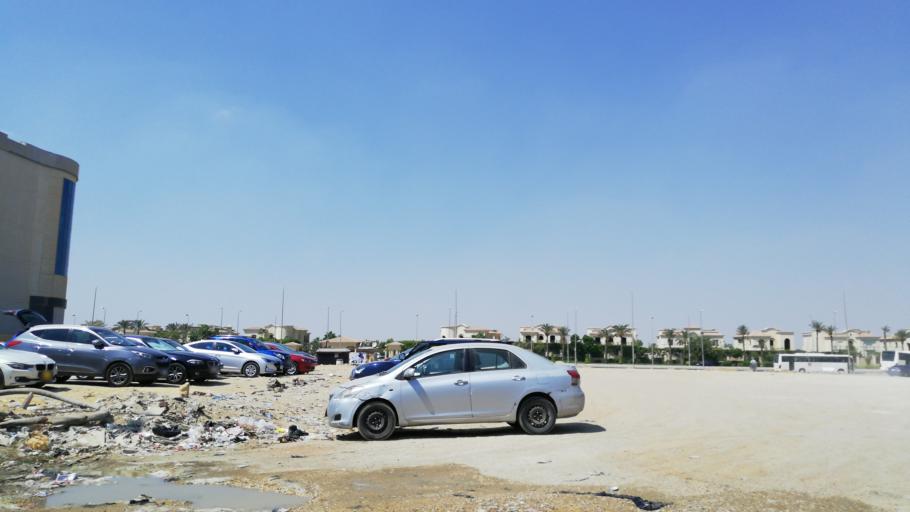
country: EG
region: Muhafazat al Qalyubiyah
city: Al Khankah
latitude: 30.0275
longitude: 31.4896
